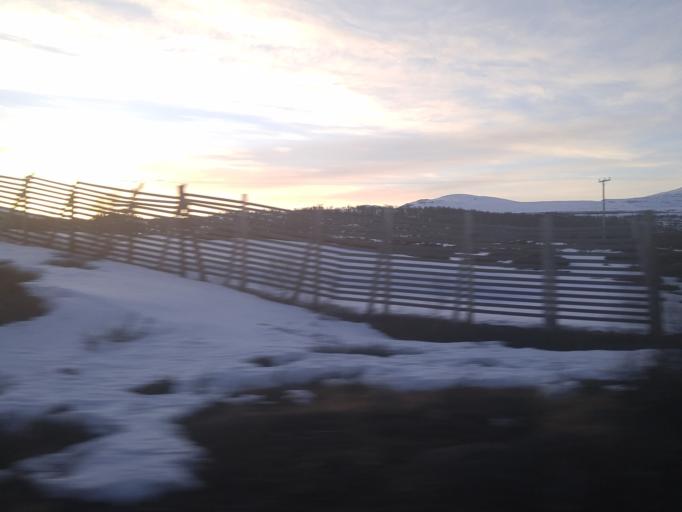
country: NO
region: Sor-Trondelag
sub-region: Oppdal
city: Oppdal
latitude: 62.2803
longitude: 9.5884
